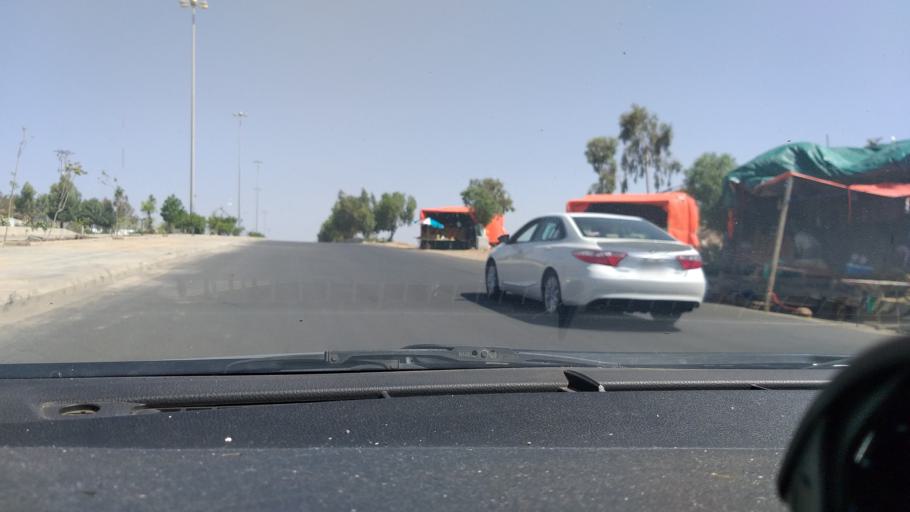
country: SA
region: Makkah
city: Ash Shafa
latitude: 21.0816
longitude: 40.3153
